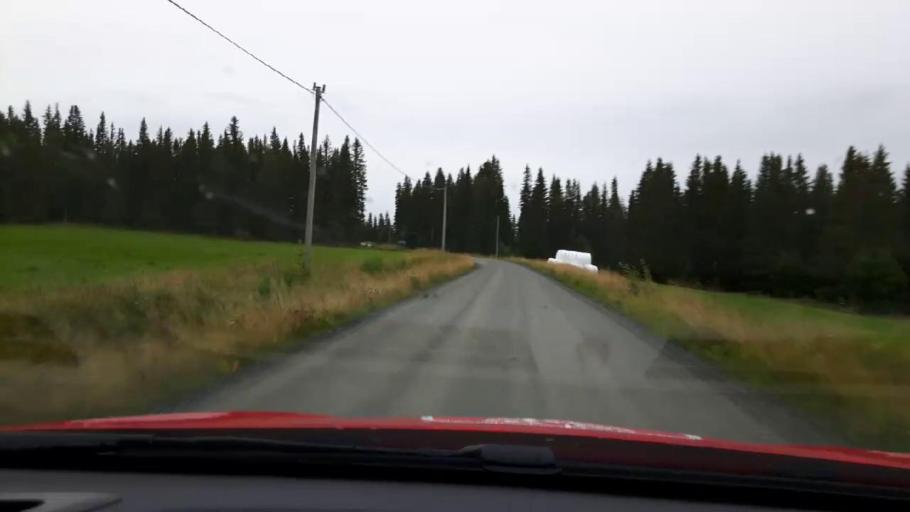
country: SE
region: Jaemtland
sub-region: Are Kommun
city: Are
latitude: 63.4282
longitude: 12.8049
